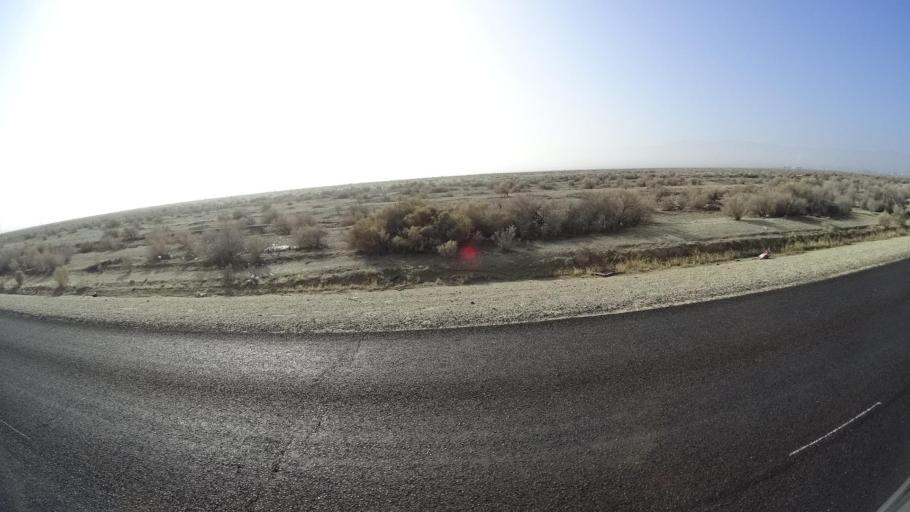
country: US
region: California
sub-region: Kern County
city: Ford City
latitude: 35.1805
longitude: -119.4958
